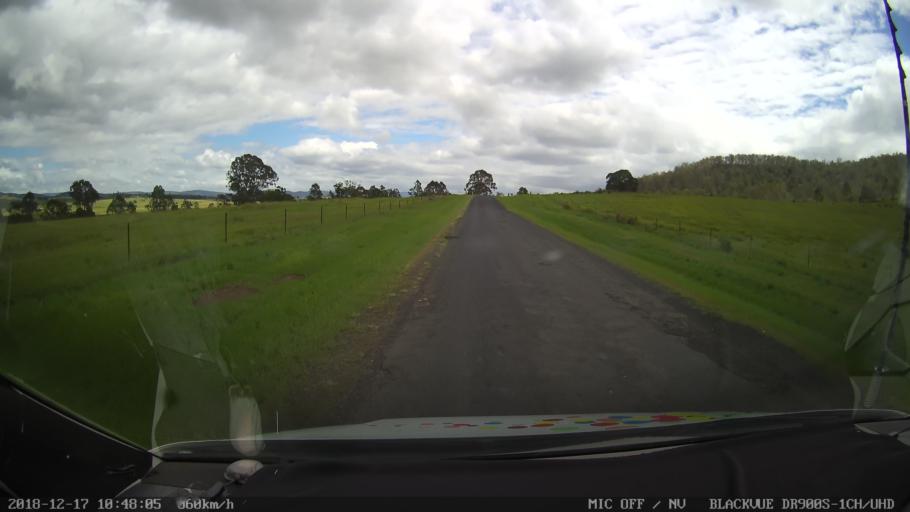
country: AU
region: New South Wales
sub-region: Clarence Valley
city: Gordon
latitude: -28.8757
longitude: 152.5706
